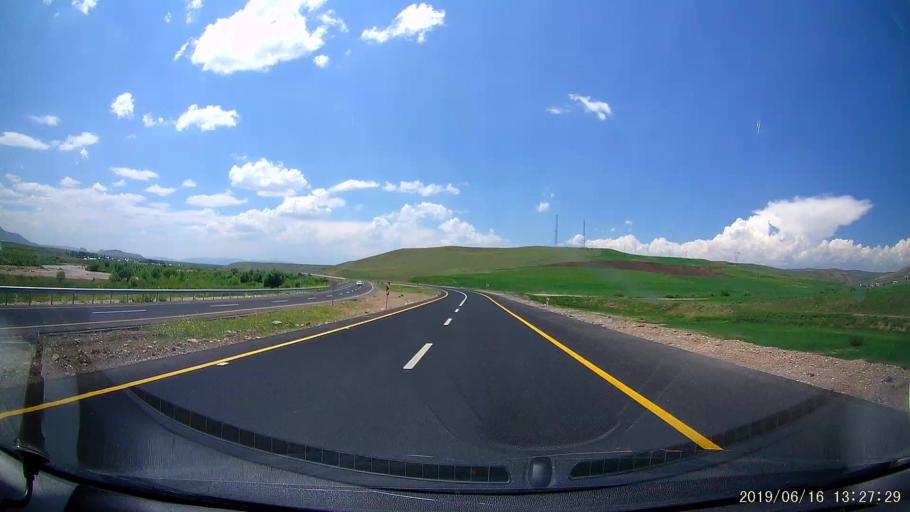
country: TR
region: Agri
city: Murat
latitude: 39.6712
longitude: 43.3097
